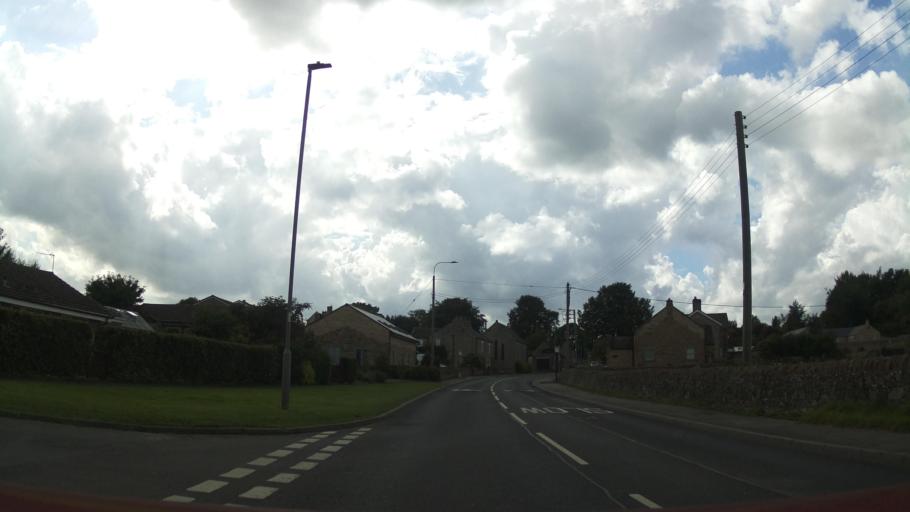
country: GB
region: England
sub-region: North Yorkshire
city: Catterick Garrison
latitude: 54.4194
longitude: -1.6894
